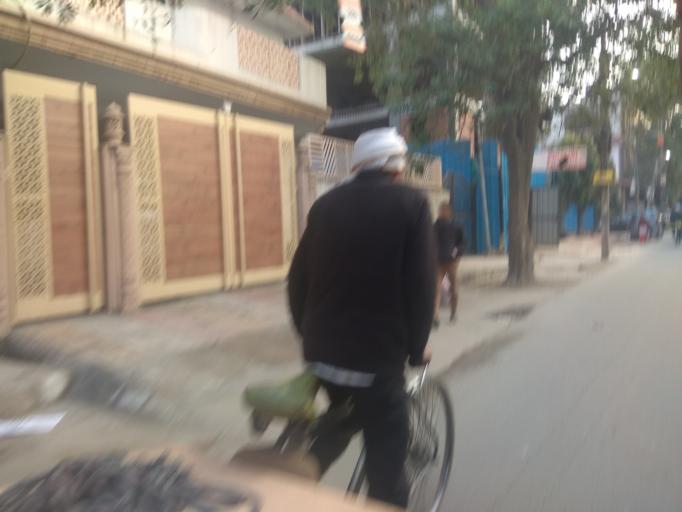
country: IN
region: NCT
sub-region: West Delhi
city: Nangloi Jat
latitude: 28.6314
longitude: 77.0765
